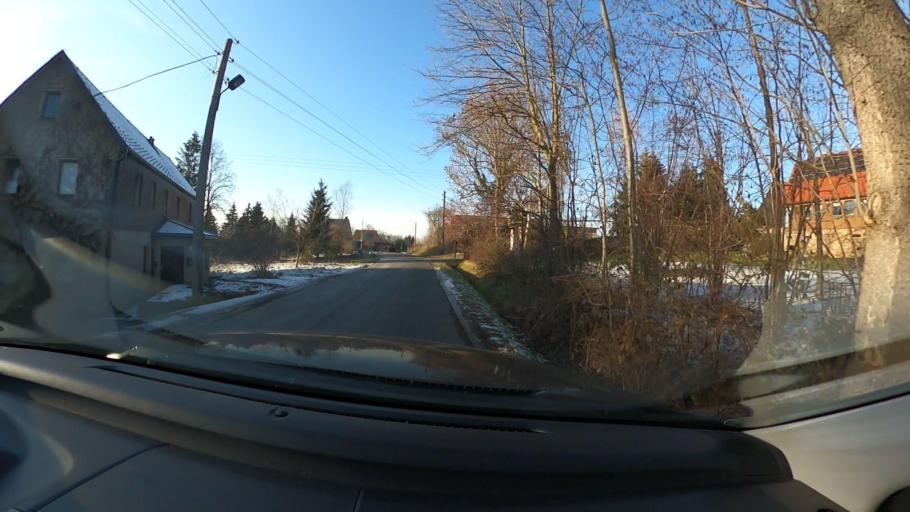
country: DE
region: Saxony
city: Grossschirma
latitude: 50.9391
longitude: 13.2591
